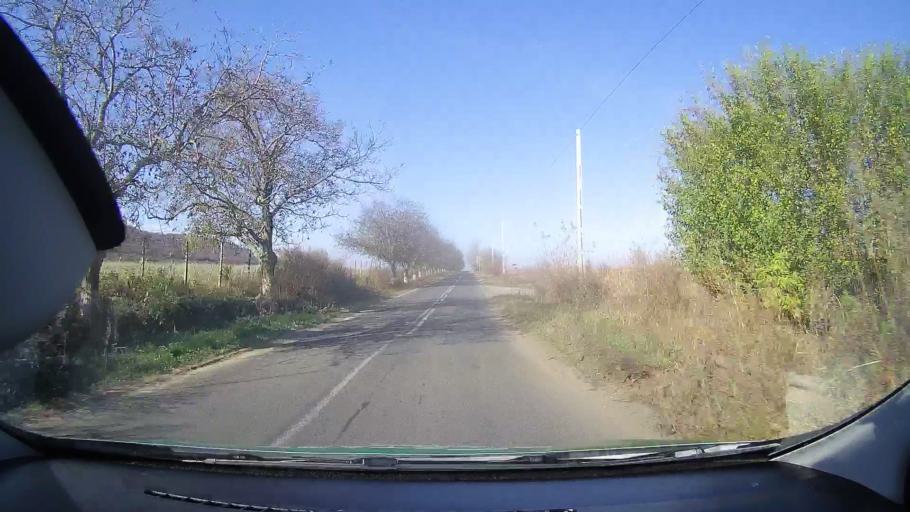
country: RO
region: Tulcea
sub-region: Oras Babadag
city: Babadag
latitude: 44.8807
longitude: 28.7458
